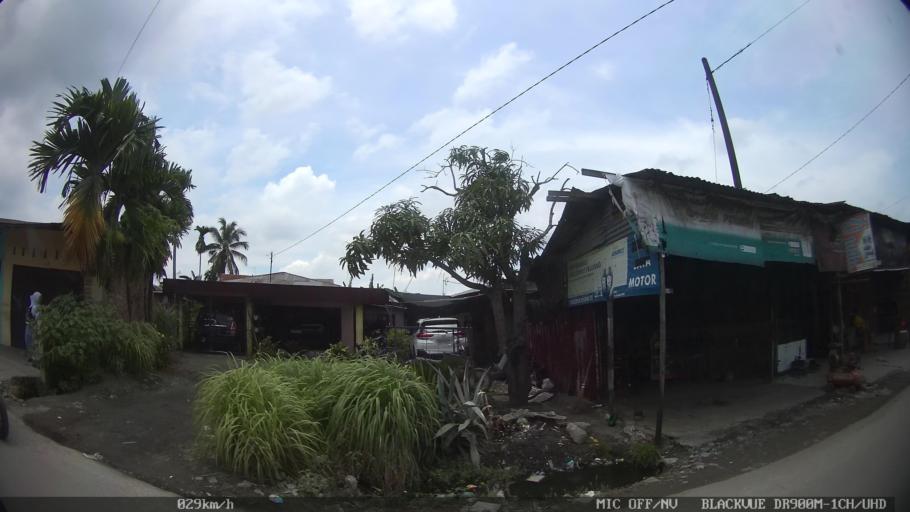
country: ID
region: North Sumatra
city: Labuhan Deli
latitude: 3.6799
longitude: 98.6872
